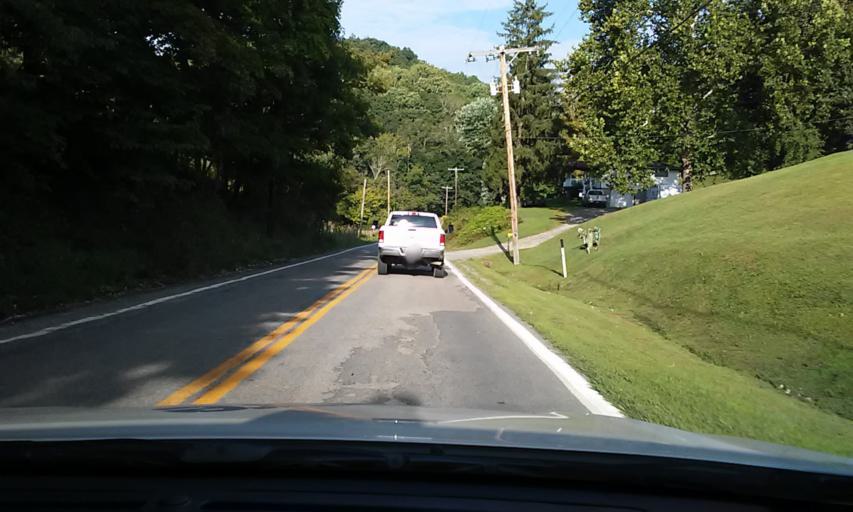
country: US
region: Pennsylvania
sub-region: Greene County
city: Morrisville
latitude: 39.7119
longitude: -80.1869
